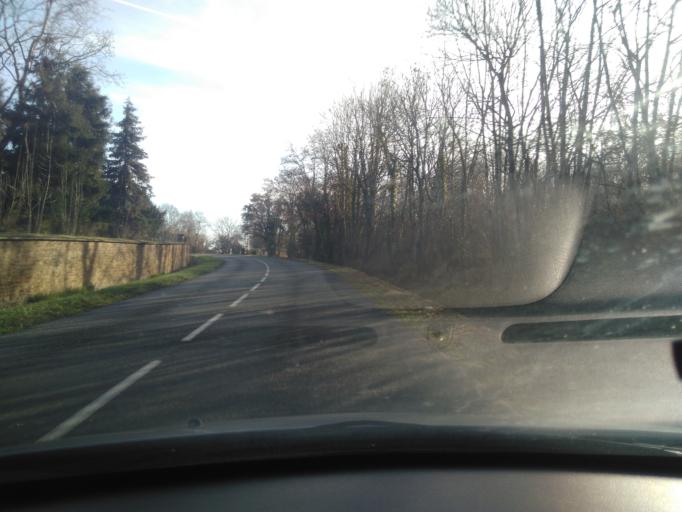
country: FR
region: Centre
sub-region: Departement du Cher
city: Le Chatelet
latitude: 46.6527
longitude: 2.3782
